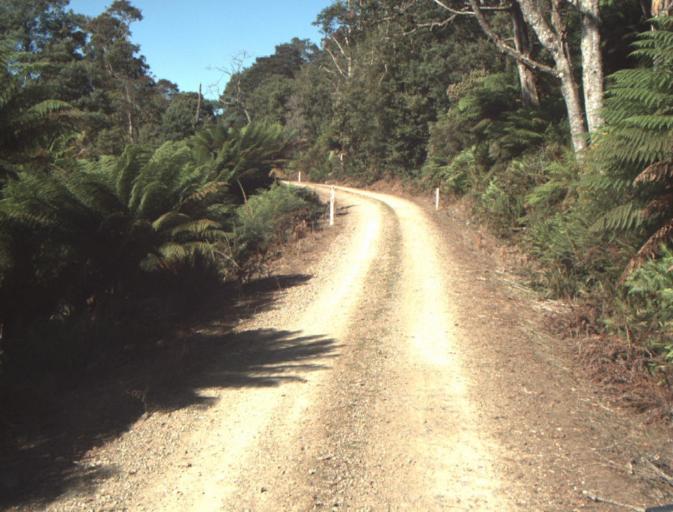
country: AU
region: Tasmania
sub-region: Dorset
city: Scottsdale
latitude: -41.2735
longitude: 147.3635
